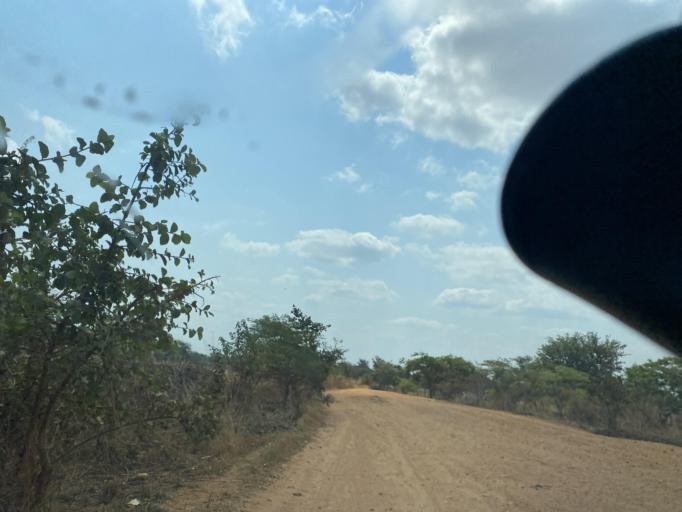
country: ZM
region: Lusaka
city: Chongwe
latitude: -15.5873
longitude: 28.7669
